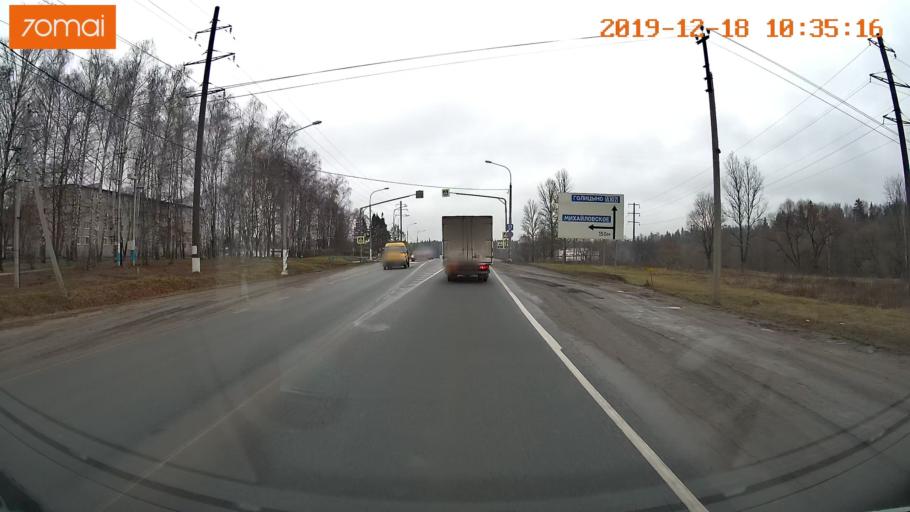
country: RU
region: Moskovskaya
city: Troitsk
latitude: 55.4133
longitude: 37.1954
